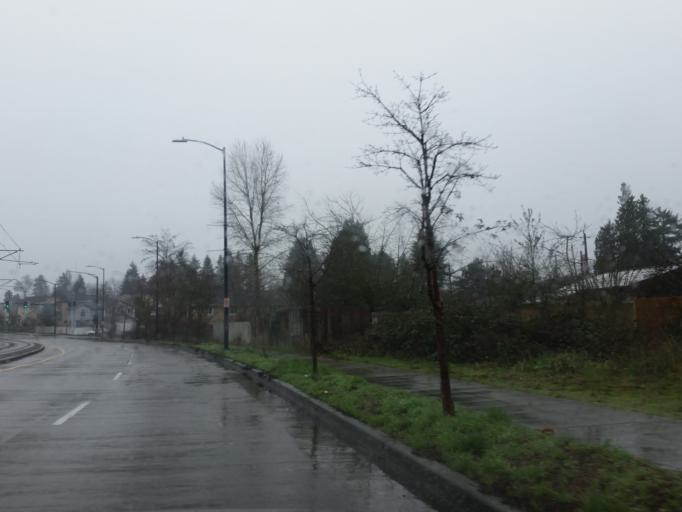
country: US
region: Washington
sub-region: King County
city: Riverton
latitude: 47.5248
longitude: -122.2787
